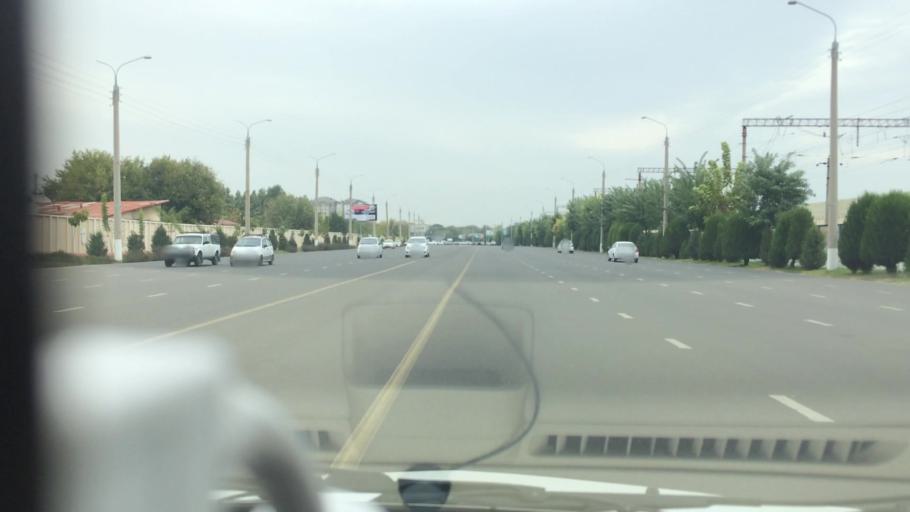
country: UZ
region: Toshkent Shahri
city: Tashkent
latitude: 41.2839
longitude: 69.2780
